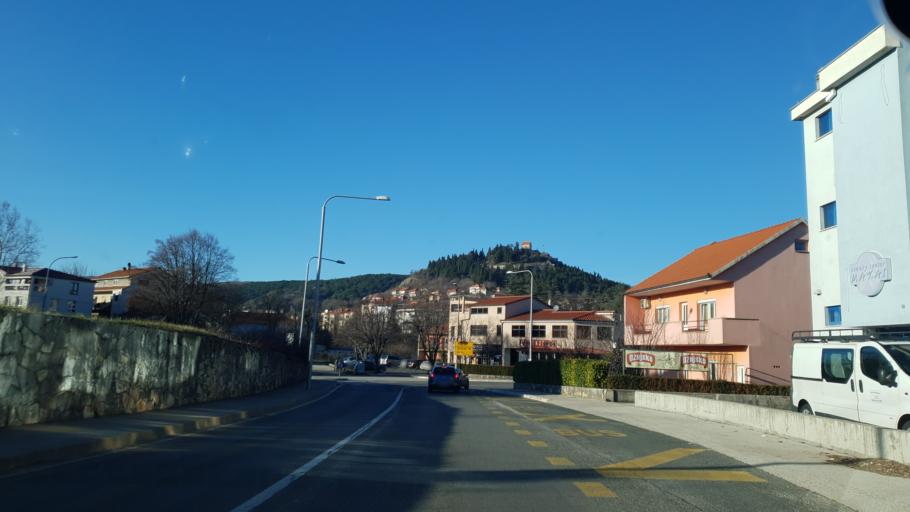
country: HR
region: Splitsko-Dalmatinska
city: Sinj
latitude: 43.6965
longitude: 16.6380
